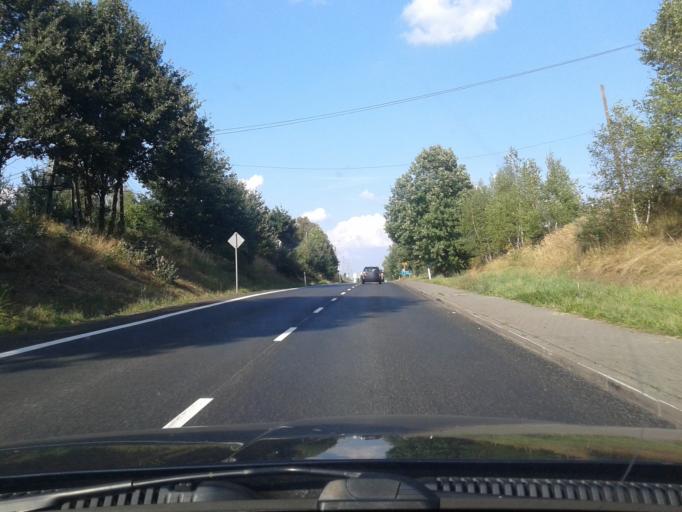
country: PL
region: Silesian Voivodeship
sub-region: Powiat wodzislawski
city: Turza Slaska
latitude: 49.9781
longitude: 18.4489
